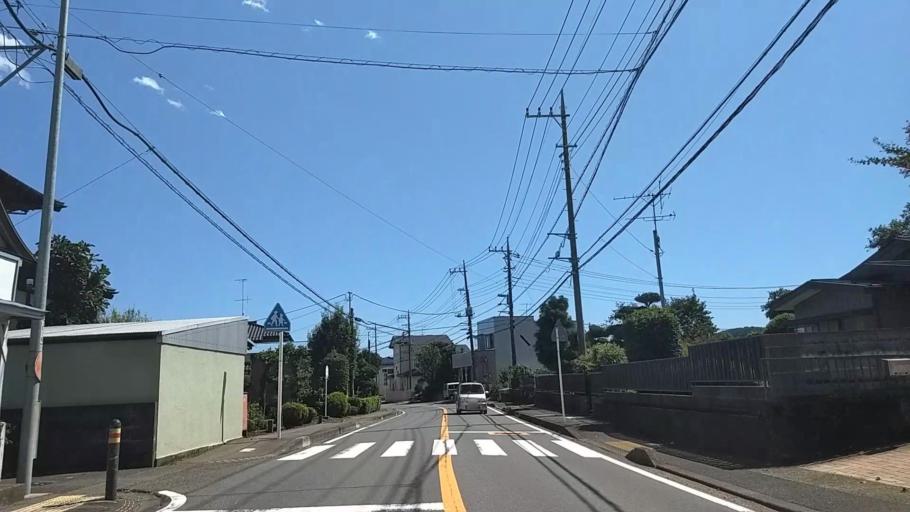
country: JP
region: Kanagawa
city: Zama
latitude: 35.5372
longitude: 139.3072
